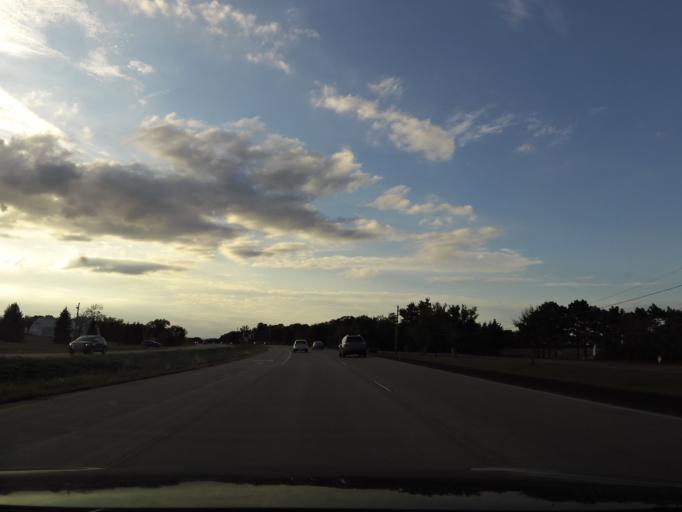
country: US
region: Minnesota
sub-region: Dakota County
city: Hastings
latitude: 44.7928
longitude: -92.8872
